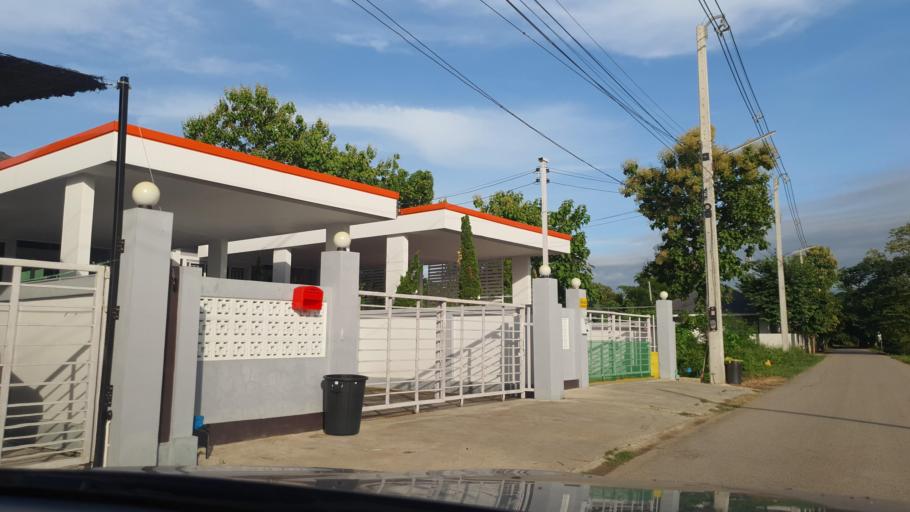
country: TH
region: Chiang Mai
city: San Kamphaeng
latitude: 18.7499
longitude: 99.1165
